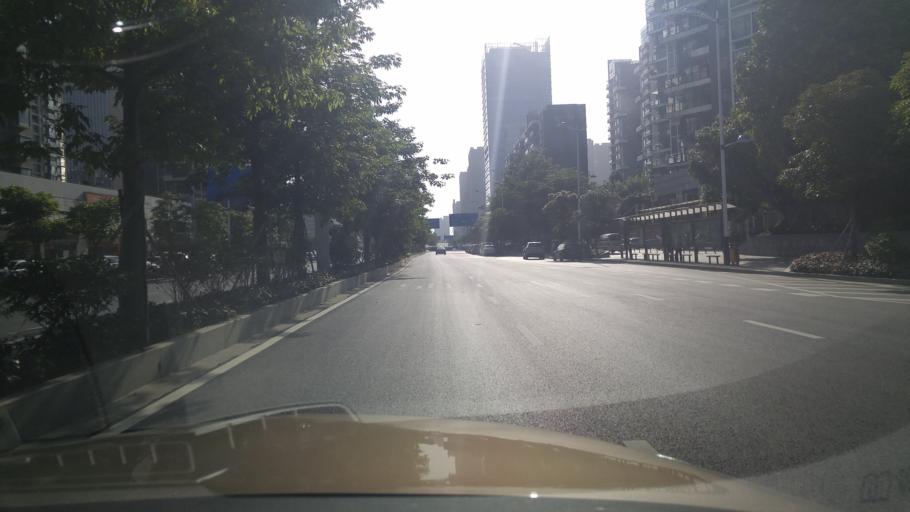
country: CN
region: Guangdong
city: Foshan
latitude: 23.0652
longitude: 113.1492
